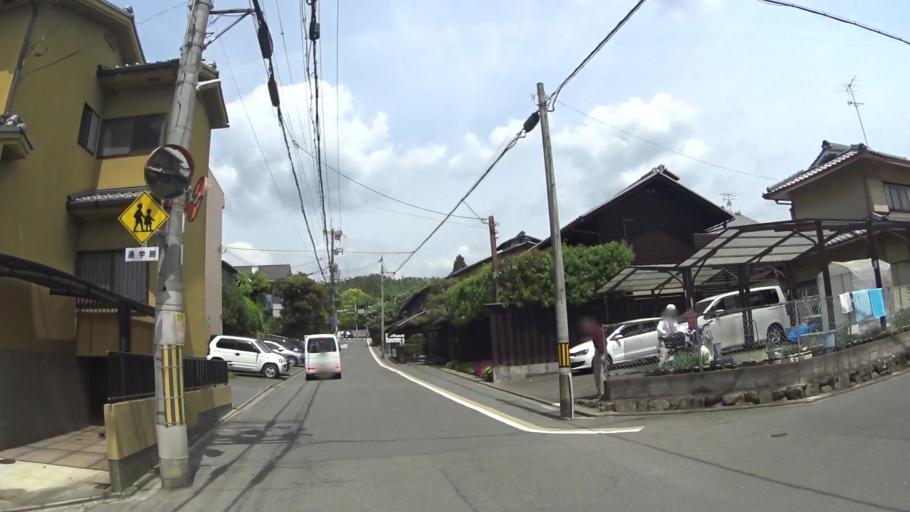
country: JP
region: Kyoto
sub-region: Kyoto-shi
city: Kamigyo-ku
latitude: 35.0532
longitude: 135.7327
